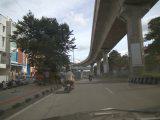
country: IN
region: Karnataka
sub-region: Bangalore Urban
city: Bangalore
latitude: 12.9995
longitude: 77.5500
